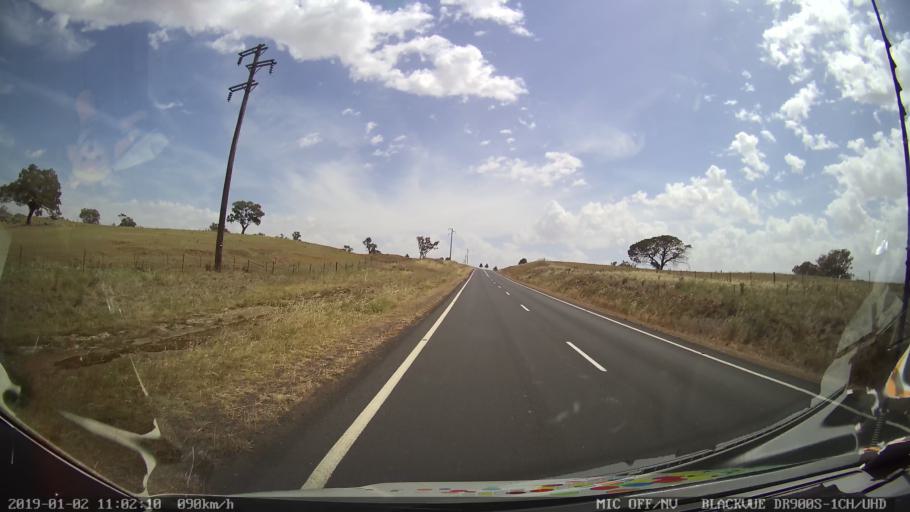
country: AU
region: New South Wales
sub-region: Young
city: Young
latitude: -34.5889
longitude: 148.3248
